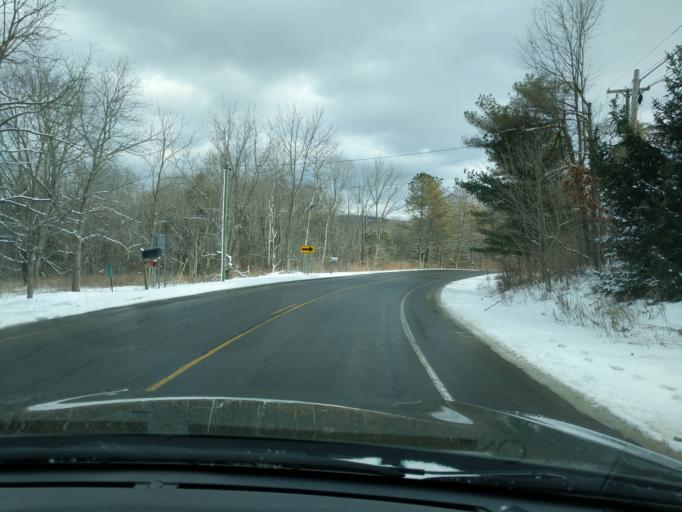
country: US
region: New York
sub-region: Tompkins County
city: Northeast Ithaca
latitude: 42.4278
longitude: -76.3957
